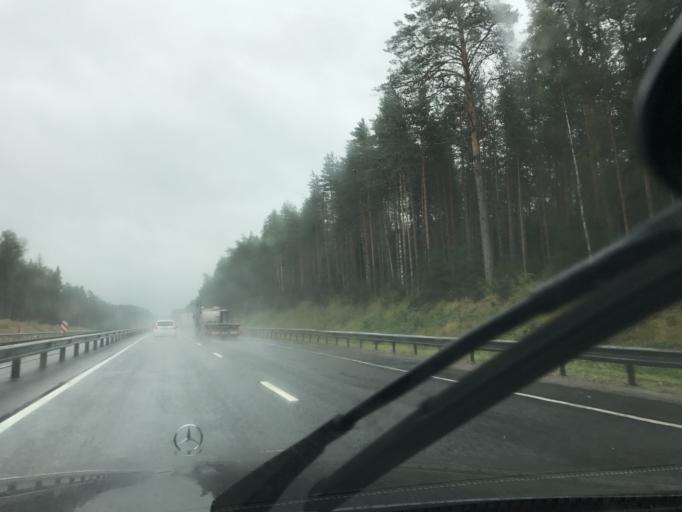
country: RU
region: Vladimir
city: Stepantsevo
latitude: 56.2312
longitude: 41.7551
